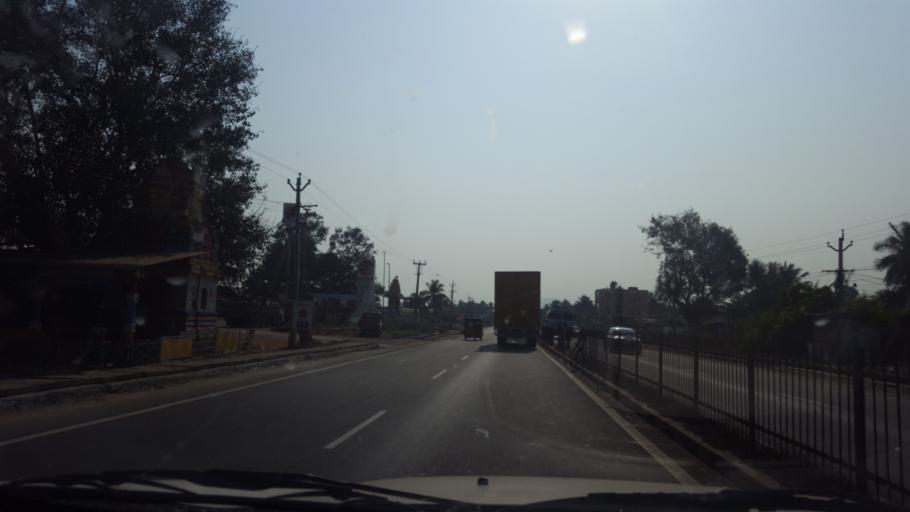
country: IN
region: Andhra Pradesh
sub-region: Vishakhapatnam
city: Anakapalle
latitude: 17.6818
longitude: 82.9829
